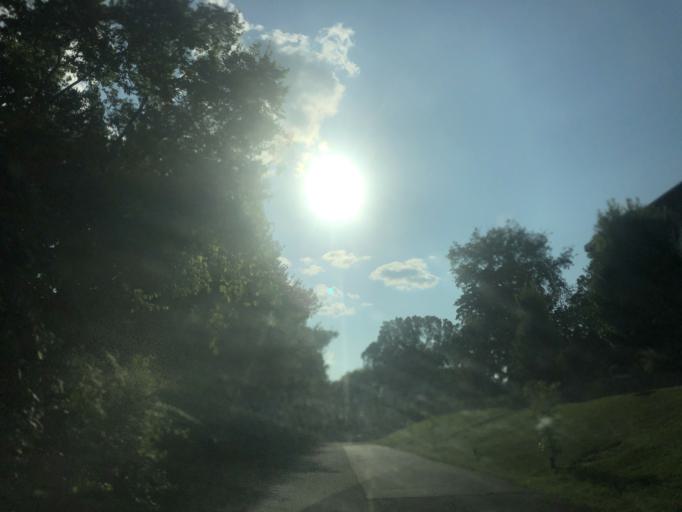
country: US
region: Tennessee
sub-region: Davidson County
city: Nashville
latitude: 36.1631
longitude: -86.7512
